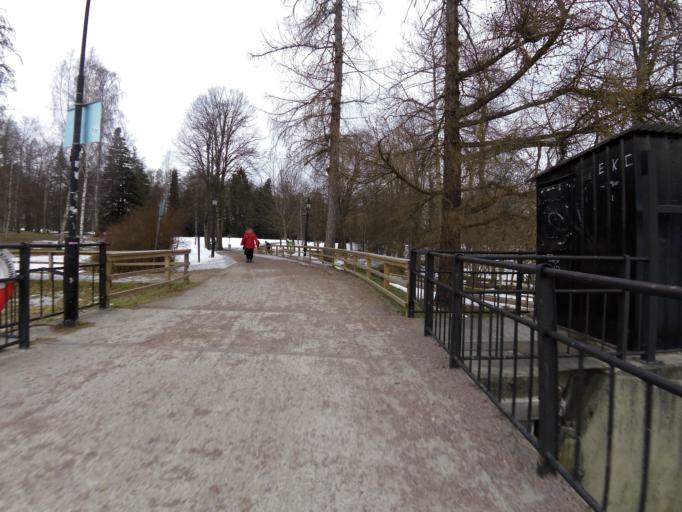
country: SE
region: Gaevleborg
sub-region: Gavle Kommun
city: Gavle
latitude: 60.6731
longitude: 17.1230
